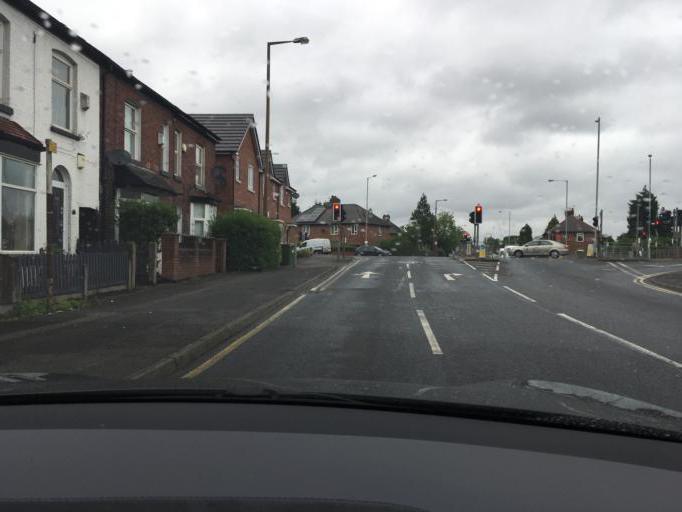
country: GB
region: England
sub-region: Borough of Stockport
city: Cheadle Hulme
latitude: 53.3864
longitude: -2.1803
